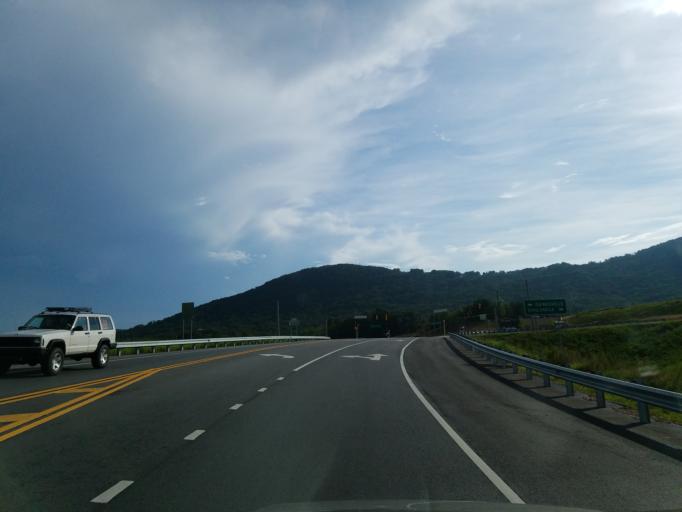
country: US
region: Georgia
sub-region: White County
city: Cleveland
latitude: 34.5798
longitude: -83.7625
